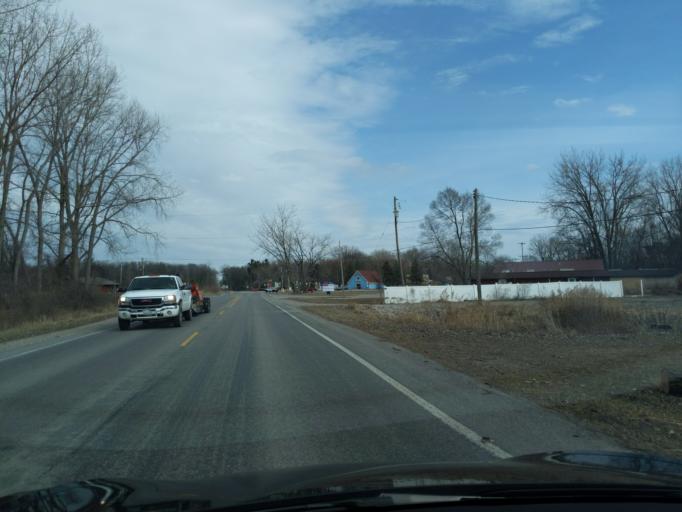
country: US
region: Michigan
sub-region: Bay County
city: Bay City
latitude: 43.6672
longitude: -83.9145
